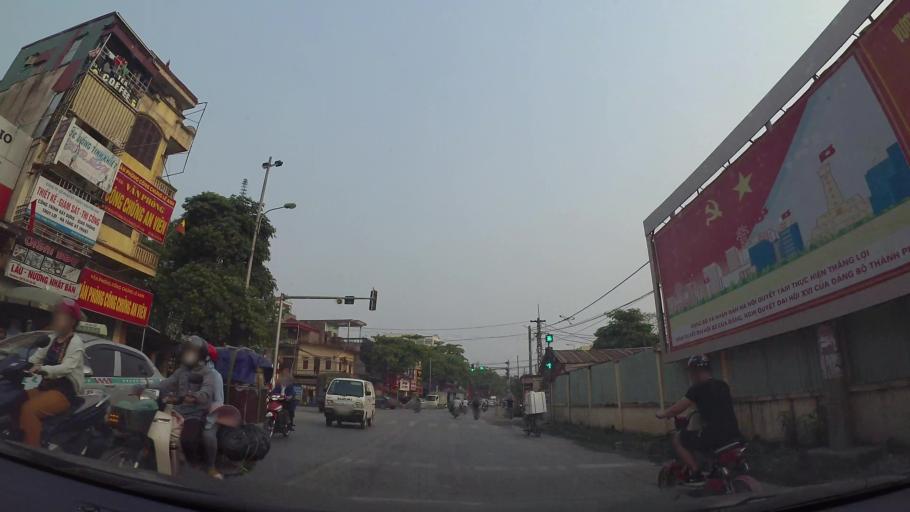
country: VN
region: Ha Noi
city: Thuong Tin
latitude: 20.8718
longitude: 105.8644
